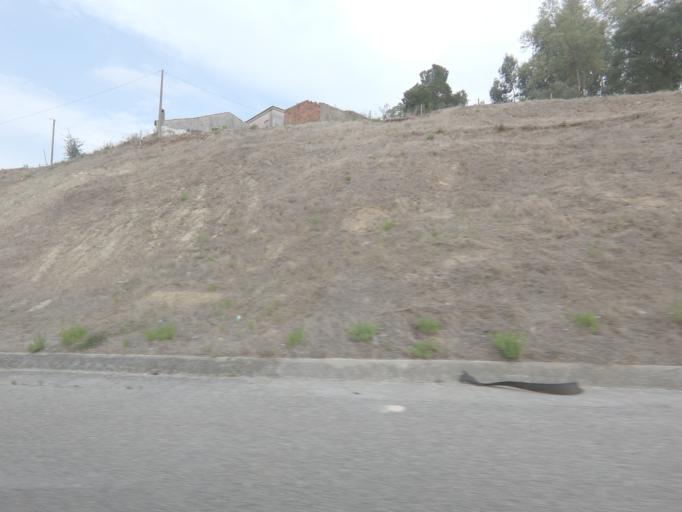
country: PT
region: Coimbra
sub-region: Coimbra
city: Coimbra
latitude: 40.2084
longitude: -8.4470
